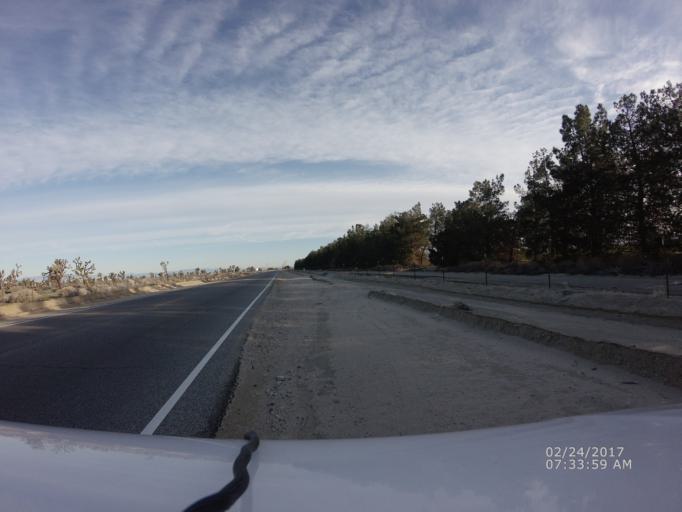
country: US
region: California
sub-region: Los Angeles County
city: Palmdale
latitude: 34.6044
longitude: -118.0409
